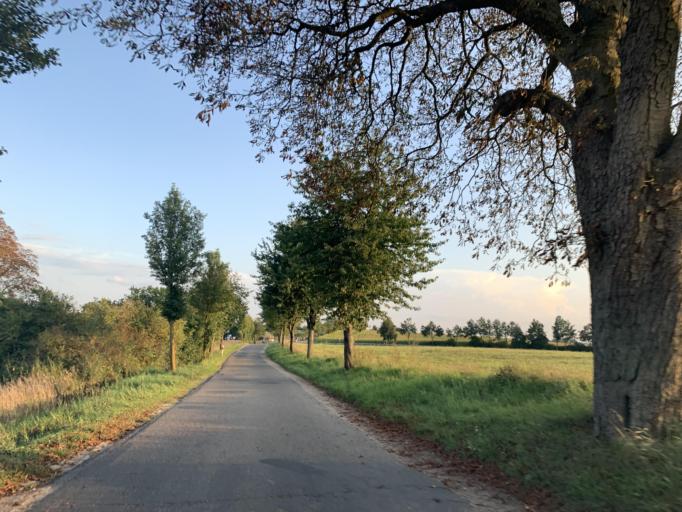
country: DE
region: Mecklenburg-Vorpommern
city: Loitz
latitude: 53.3661
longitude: 13.3847
